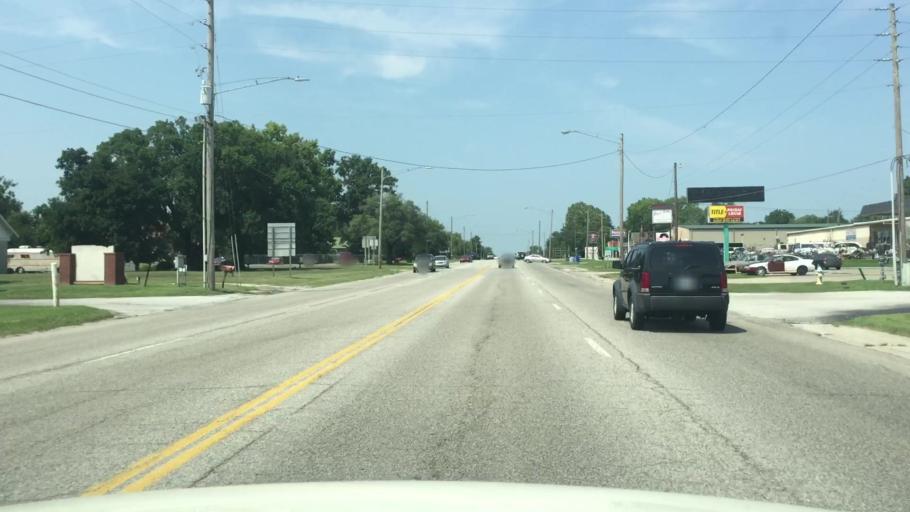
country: US
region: Kansas
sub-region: Crawford County
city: Frontenac
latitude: 37.4434
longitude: -94.7050
